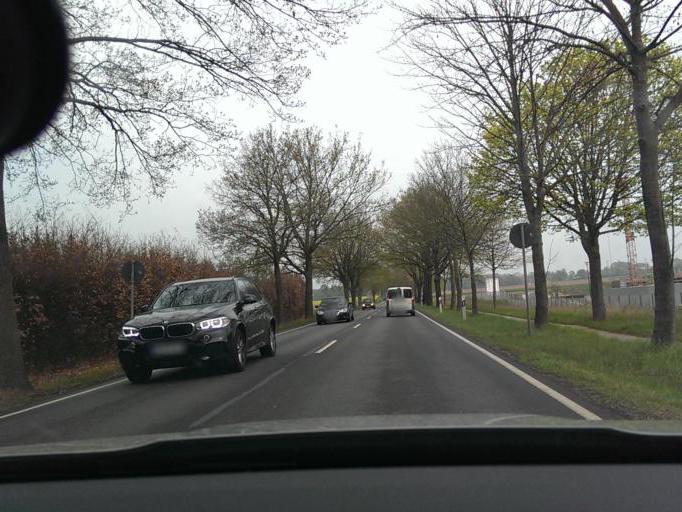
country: DE
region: Lower Saxony
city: Langenhagen
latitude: 52.5123
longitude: 9.7272
